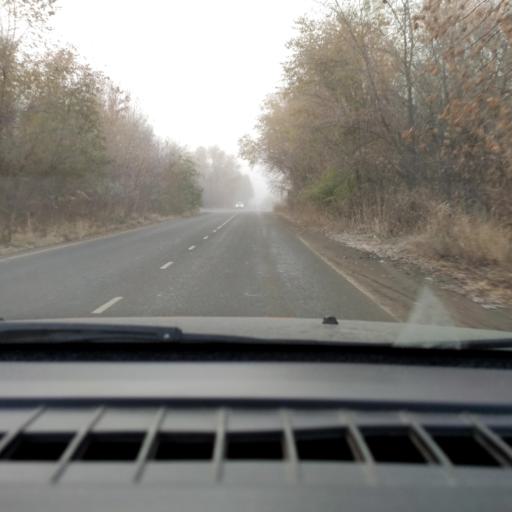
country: RU
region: Samara
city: Tol'yatti
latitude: 53.5826
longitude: 49.2565
